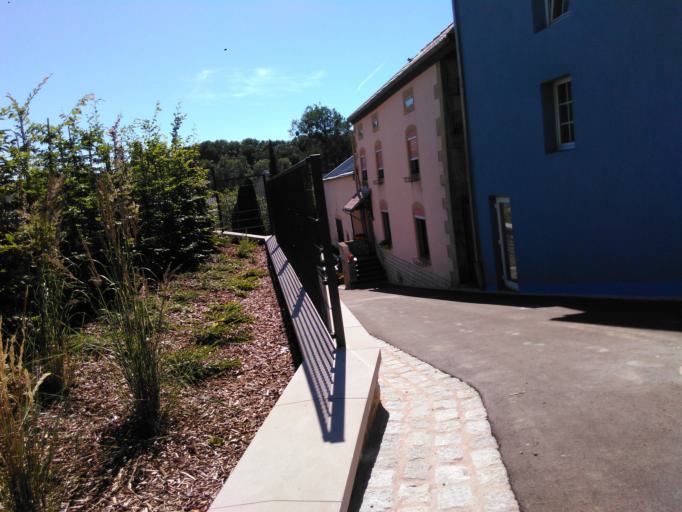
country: LU
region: Luxembourg
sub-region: Canton d'Esch-sur-Alzette
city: Reckange-sur-Mess
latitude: 49.5626
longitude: 6.0068
